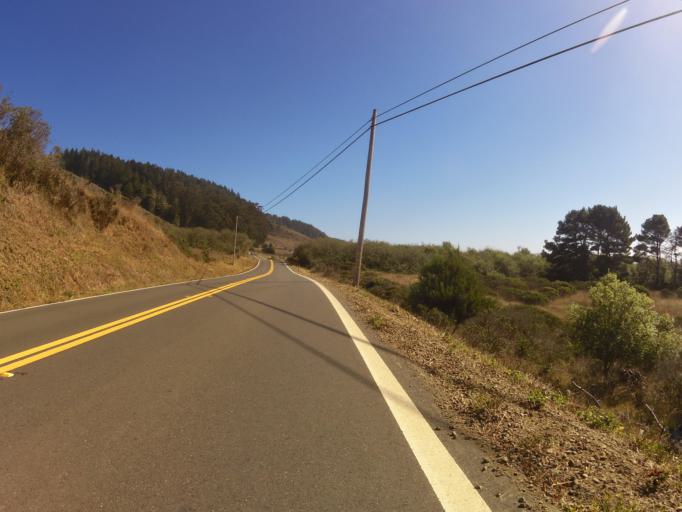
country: US
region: California
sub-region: Mendocino County
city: Fort Bragg
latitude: 39.5893
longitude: -123.7772
